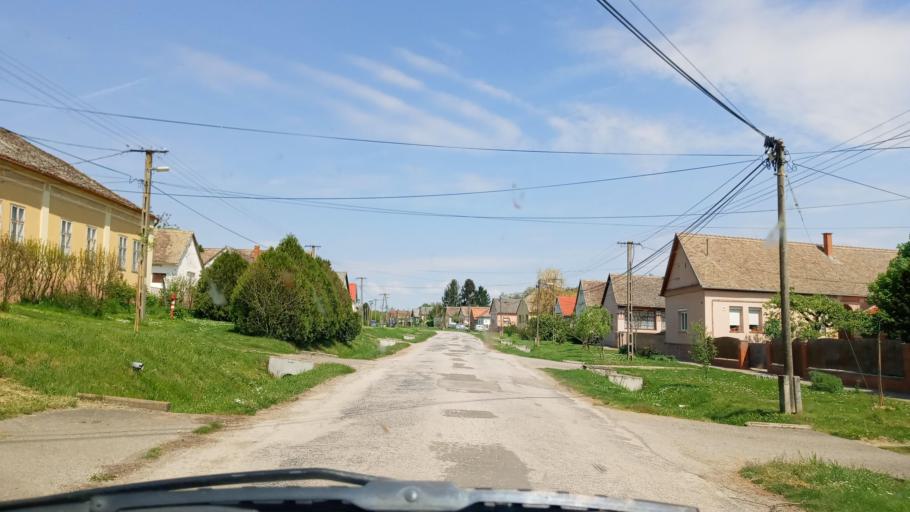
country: HR
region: Osjecko-Baranjska
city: Beli Manastir
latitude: 45.8657
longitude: 18.5857
